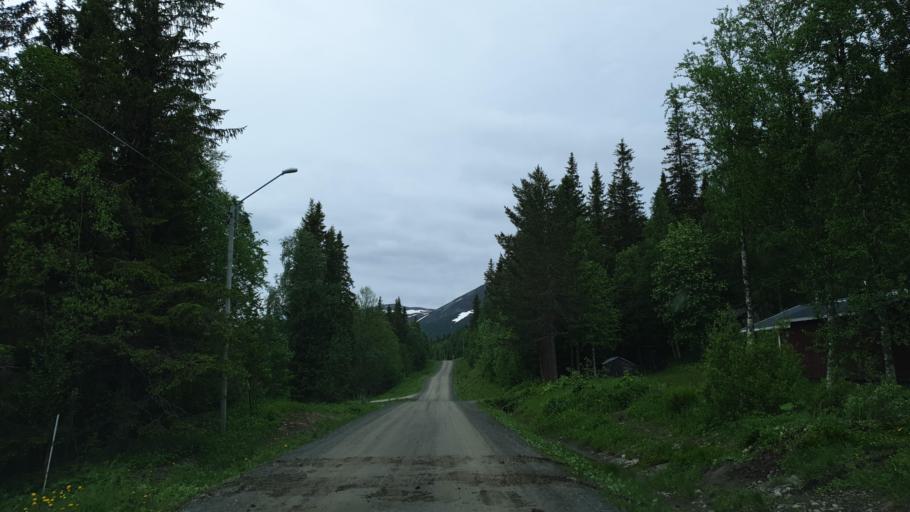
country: SE
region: Vaesterbotten
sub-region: Vilhelmina Kommun
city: Sjoberg
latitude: 65.3491
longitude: 15.8537
